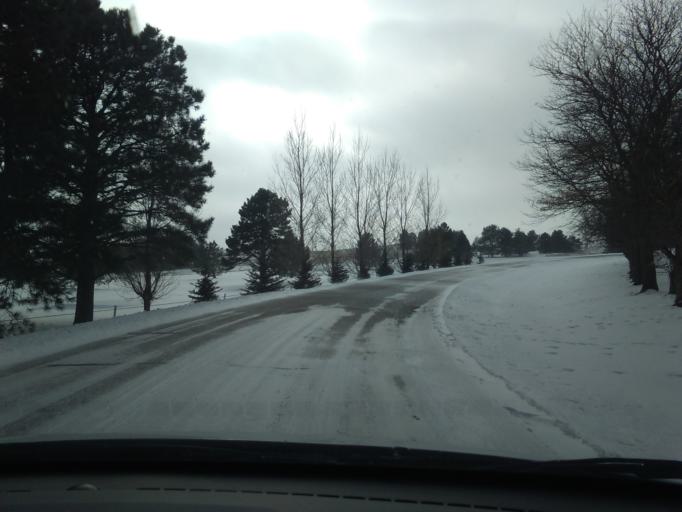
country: US
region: Nebraska
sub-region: Kimball County
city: Kimball
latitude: 41.2267
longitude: -103.6173
